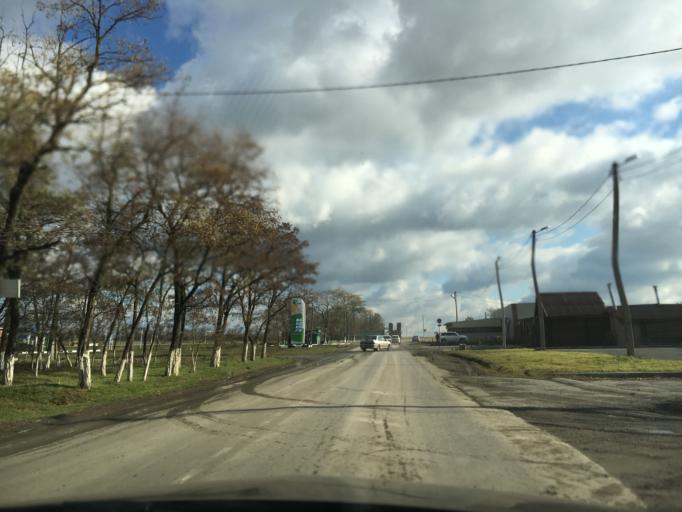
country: RU
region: Rostov
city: Matveyev Kurgan
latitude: 47.5633
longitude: 38.8855
